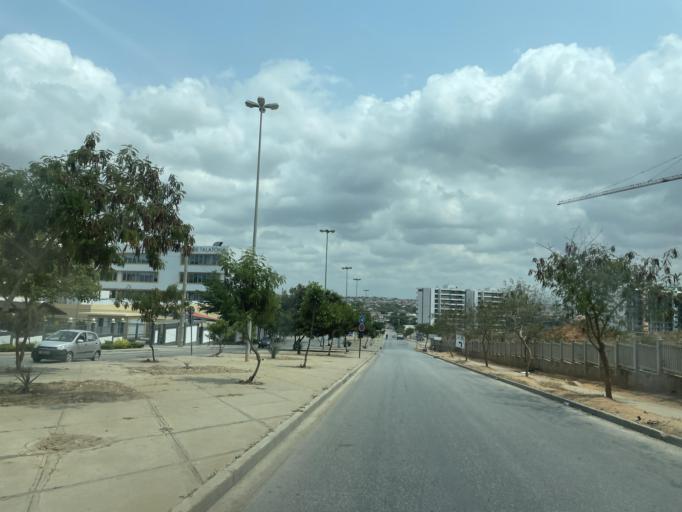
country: AO
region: Luanda
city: Luanda
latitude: -8.9230
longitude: 13.1931
